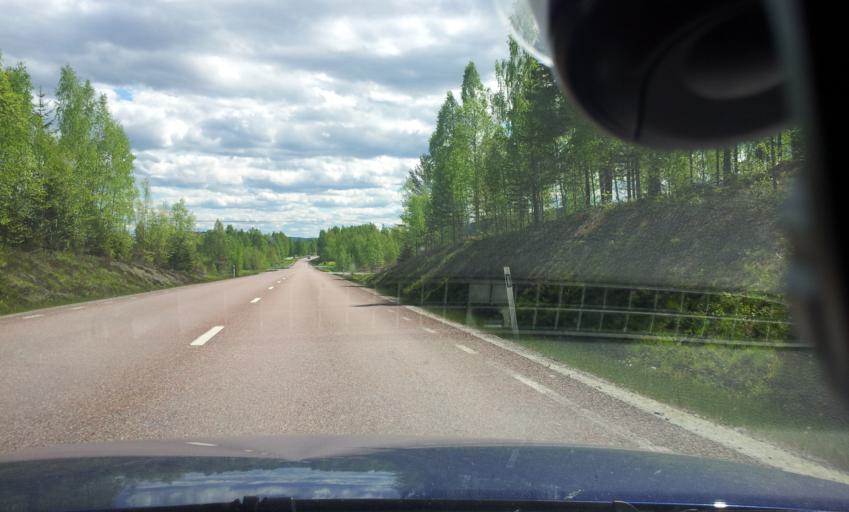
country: SE
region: Gaevleborg
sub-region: Ljusdals Kommun
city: Jaervsoe
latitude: 61.7680
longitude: 16.1567
